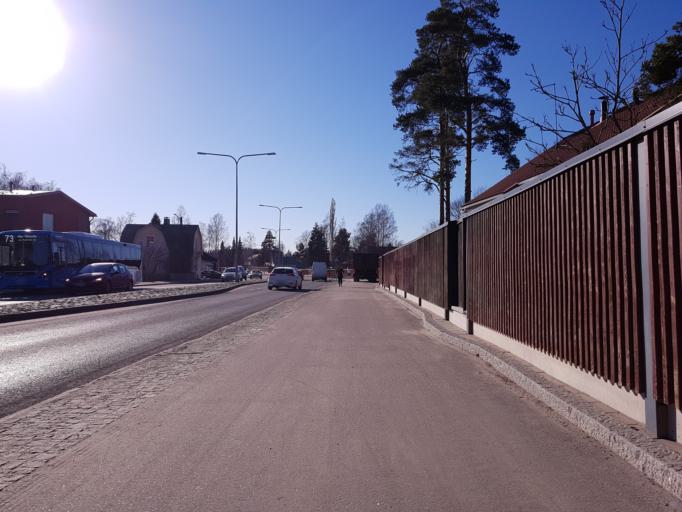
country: FI
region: Uusimaa
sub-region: Helsinki
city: Vantaa
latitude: 60.2694
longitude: 25.0258
